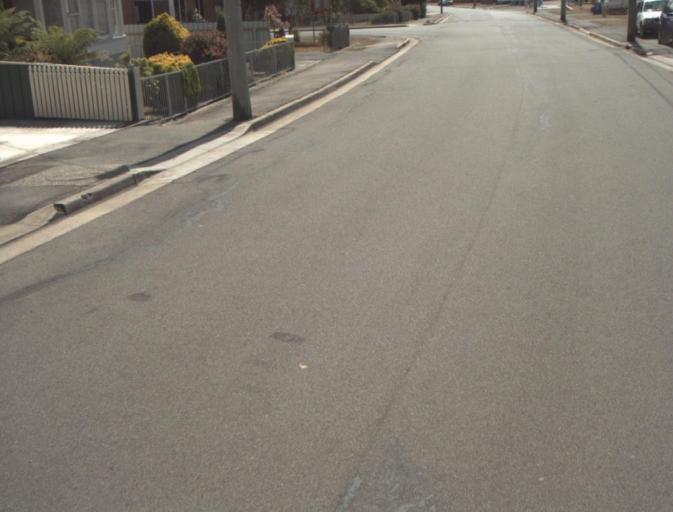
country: AU
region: Tasmania
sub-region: Launceston
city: Newstead
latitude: -41.4241
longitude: 147.1784
